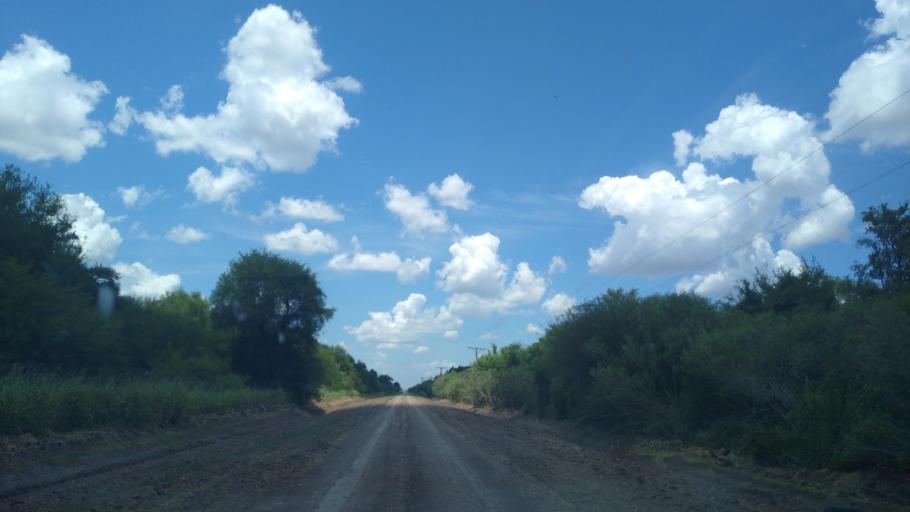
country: AR
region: Chaco
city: Presidencia Roque Saenz Pena
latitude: -26.7450
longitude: -60.3352
